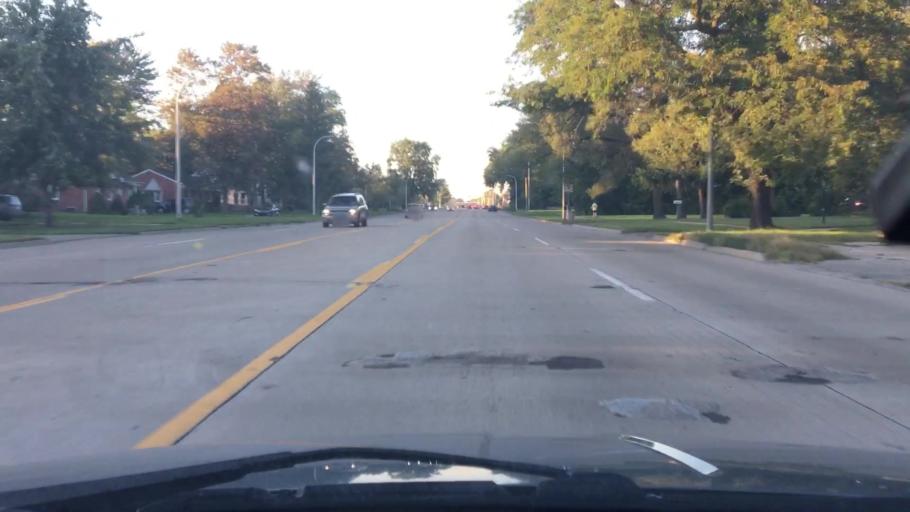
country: US
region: Michigan
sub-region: Wayne County
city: Livonia
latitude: 42.3646
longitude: -83.3522
